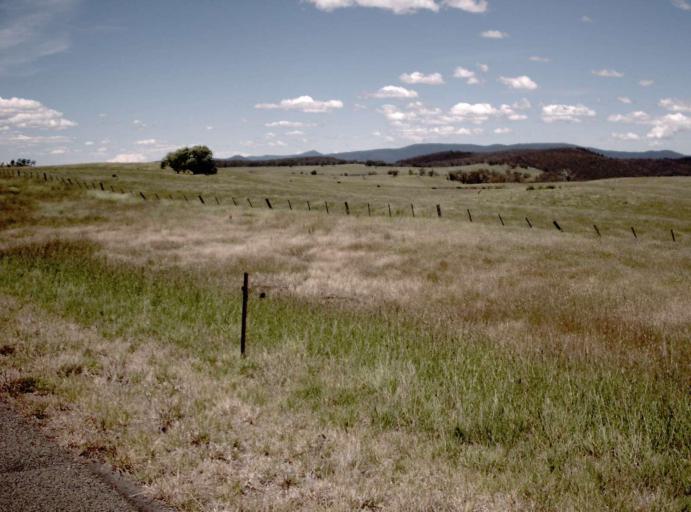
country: AU
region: New South Wales
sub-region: Snowy River
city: Jindabyne
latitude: -37.0984
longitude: 148.2554
